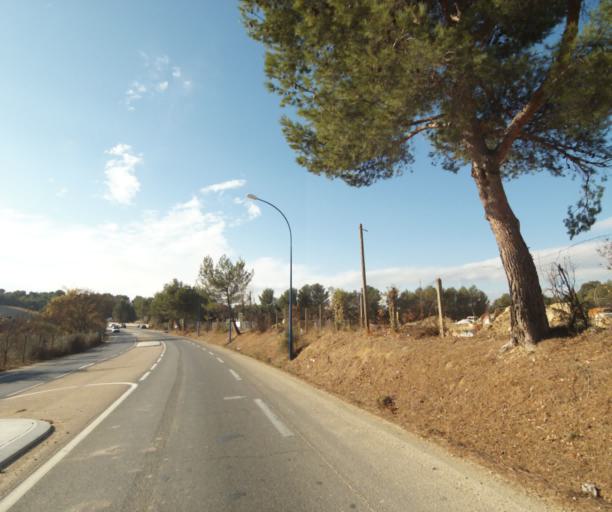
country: FR
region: Provence-Alpes-Cote d'Azur
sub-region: Departement des Bouches-du-Rhone
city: Allauch
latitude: 43.3224
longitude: 5.4694
